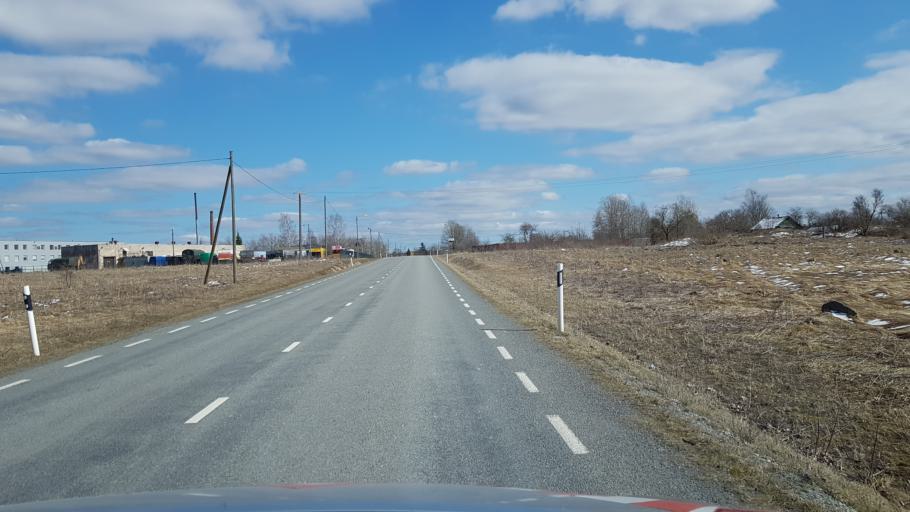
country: EE
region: Laeaene-Virumaa
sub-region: Tapa vald
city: Tapa
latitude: 59.2689
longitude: 25.9455
